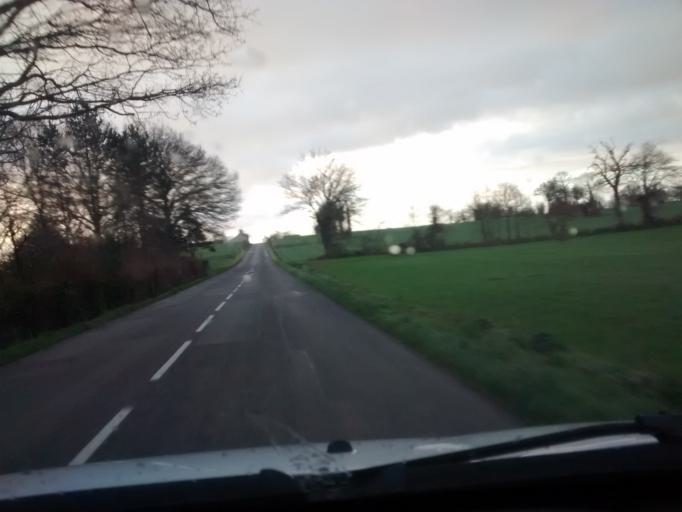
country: FR
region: Brittany
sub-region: Departement d'Ille-et-Vilaine
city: Domalain
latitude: 47.9728
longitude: -1.2688
